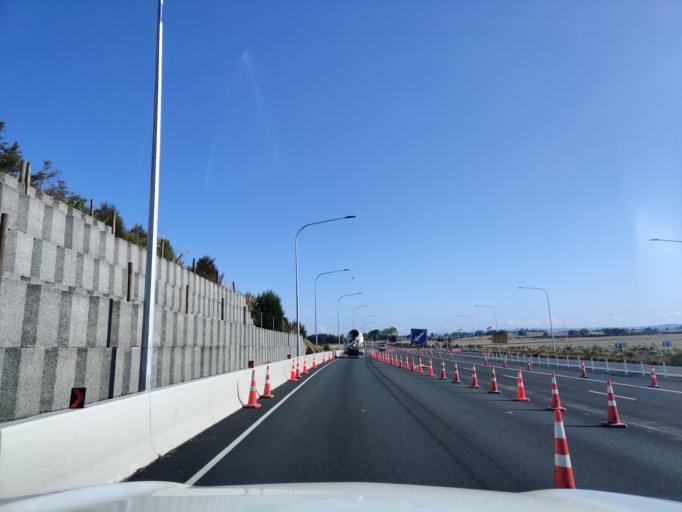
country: NZ
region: Waikato
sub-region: Waikato District
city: Te Kauwhata
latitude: -37.5074
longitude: 175.1658
